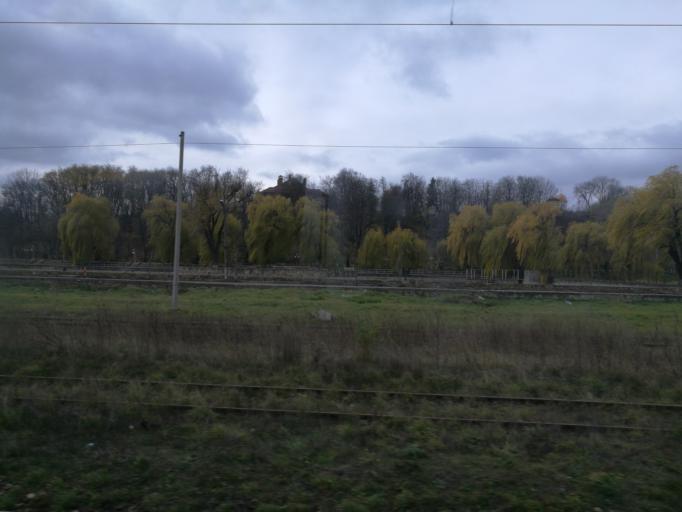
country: RO
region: Iasi
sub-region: Municipiul Pascani
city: Pascani
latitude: 47.2464
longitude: 26.7305
